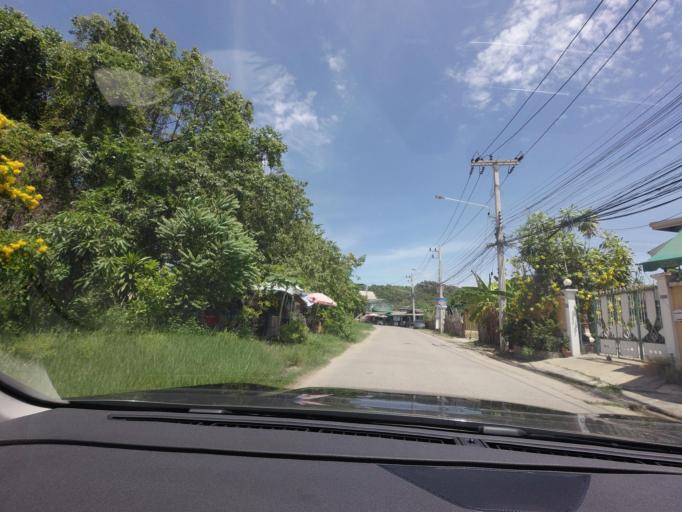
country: TH
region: Prachuap Khiri Khan
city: Hua Hin
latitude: 12.5153
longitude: 99.9738
